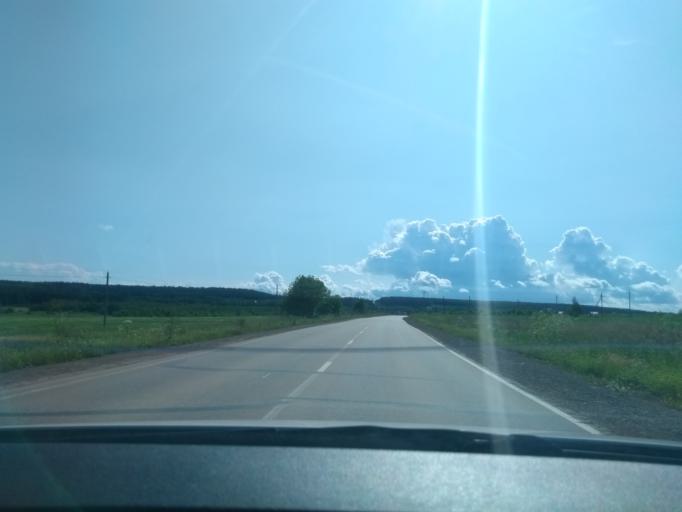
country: RU
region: Perm
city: Lobanovo
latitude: 57.8481
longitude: 56.3497
